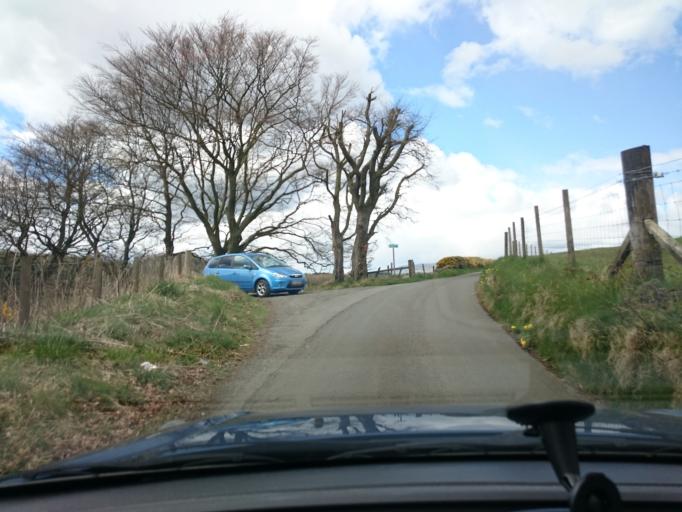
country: GB
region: Scotland
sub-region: Falkirk
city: Bonnybridge
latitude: 55.9757
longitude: -3.9063
